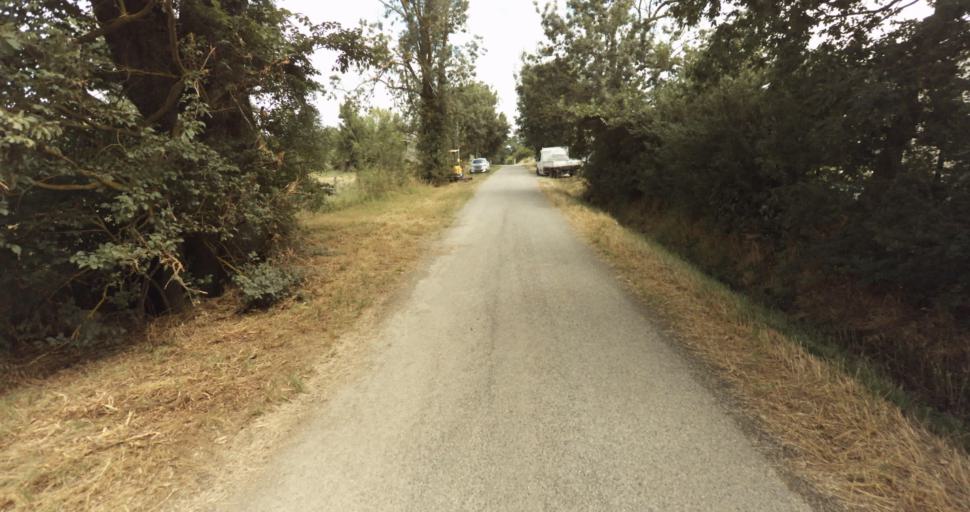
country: FR
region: Midi-Pyrenees
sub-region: Departement de la Haute-Garonne
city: Fontenilles
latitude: 43.5495
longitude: 1.1889
